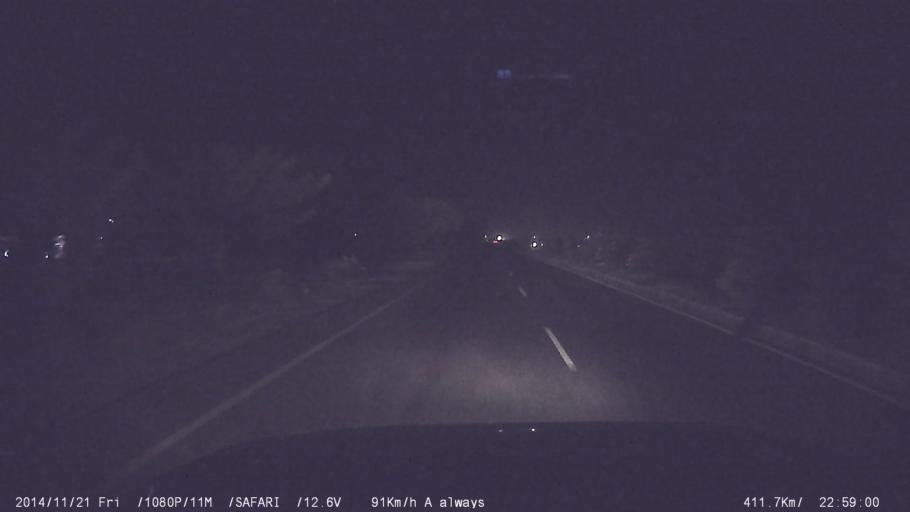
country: IN
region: Tamil Nadu
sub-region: Villupuram
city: Vikravandi
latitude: 12.0809
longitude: 79.5548
